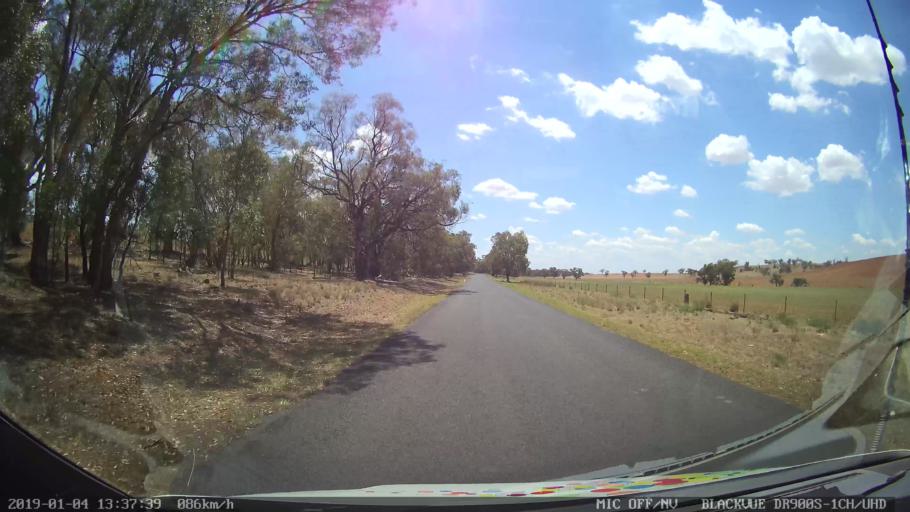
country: AU
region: New South Wales
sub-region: Dubbo Municipality
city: Dubbo
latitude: -32.5474
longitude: 148.5448
